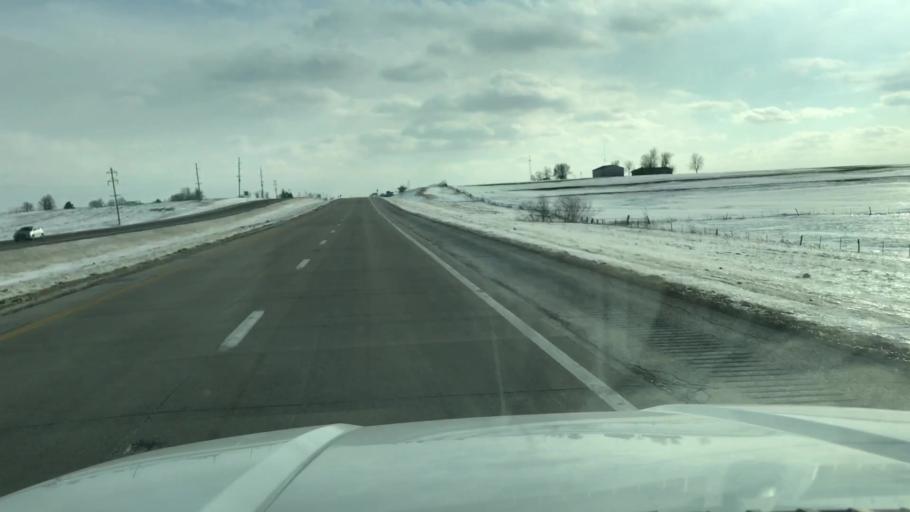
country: US
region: Missouri
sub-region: Nodaway County
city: Maryville
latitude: 40.2638
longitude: -94.8670
